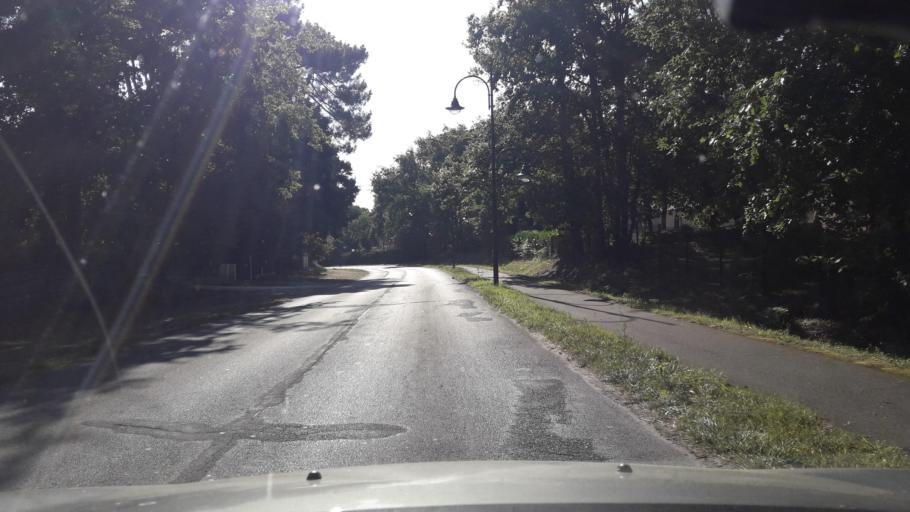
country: FR
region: Poitou-Charentes
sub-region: Departement de la Charente-Maritime
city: Les Mathes
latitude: 45.7134
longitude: -1.1402
